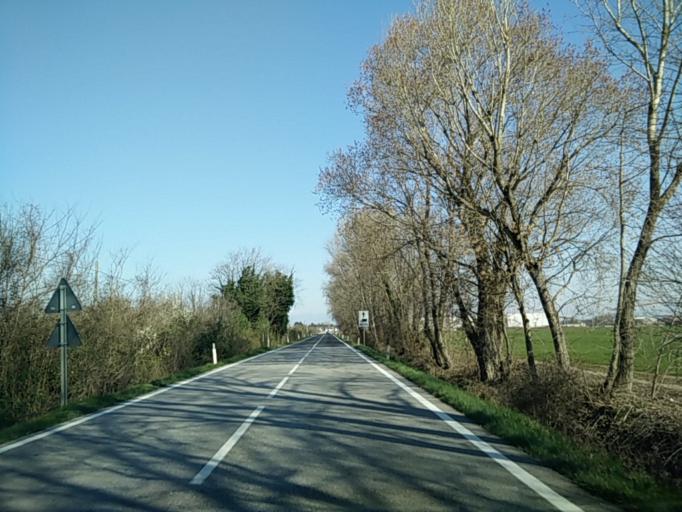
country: IT
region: Friuli Venezia Giulia
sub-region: Provincia di Udine
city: Camino al Tagliamento
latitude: 45.9756
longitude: 12.9292
